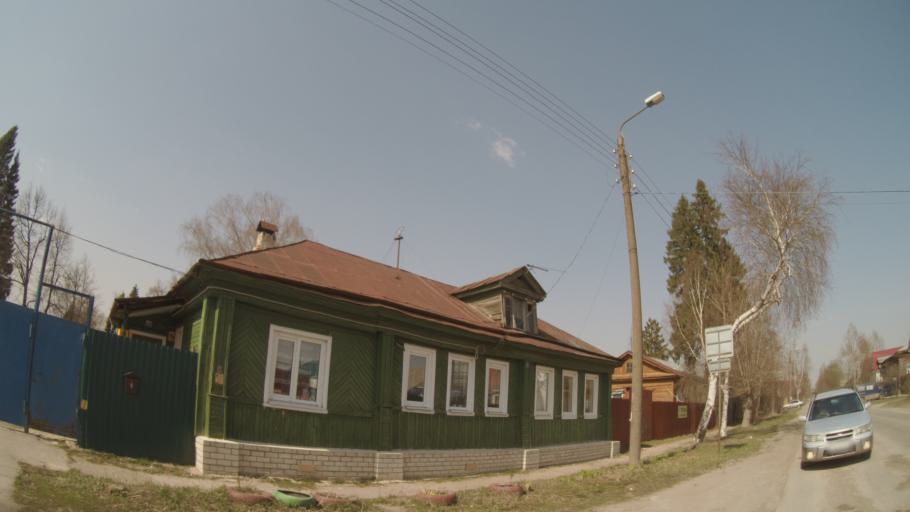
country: RU
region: Nizjnij Novgorod
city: Arzamas
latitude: 55.3893
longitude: 43.8249
